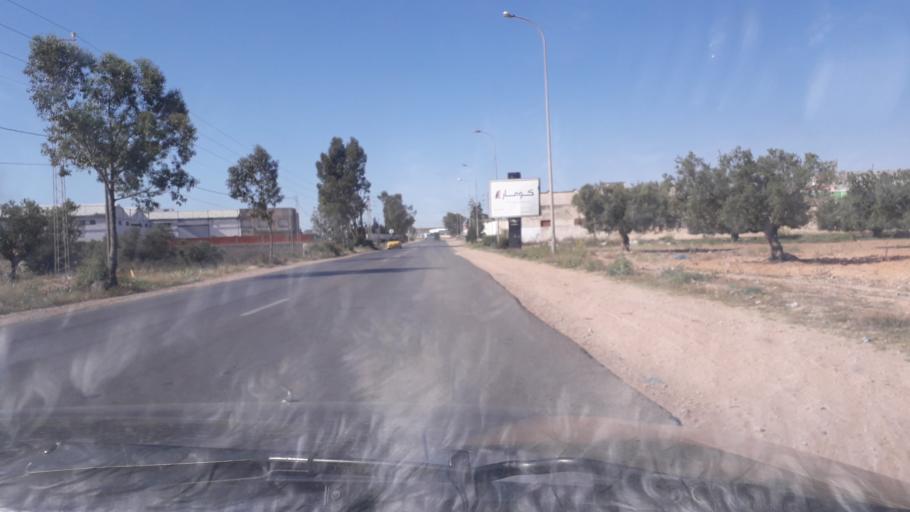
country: TN
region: Safaqis
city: Al Qarmadah
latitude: 34.8810
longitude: 10.7594
